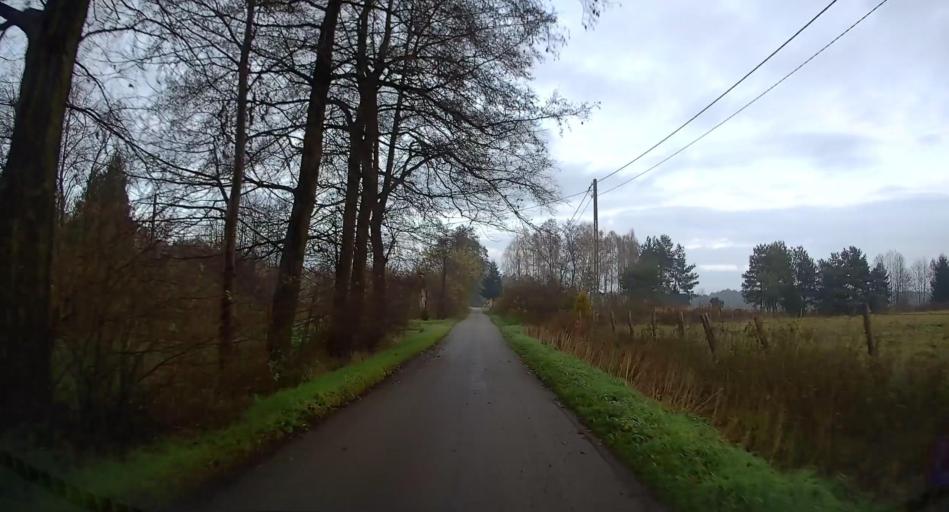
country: PL
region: Lodz Voivodeship
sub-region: Powiat skierniewicki
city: Kowiesy
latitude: 51.9353
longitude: 20.4019
